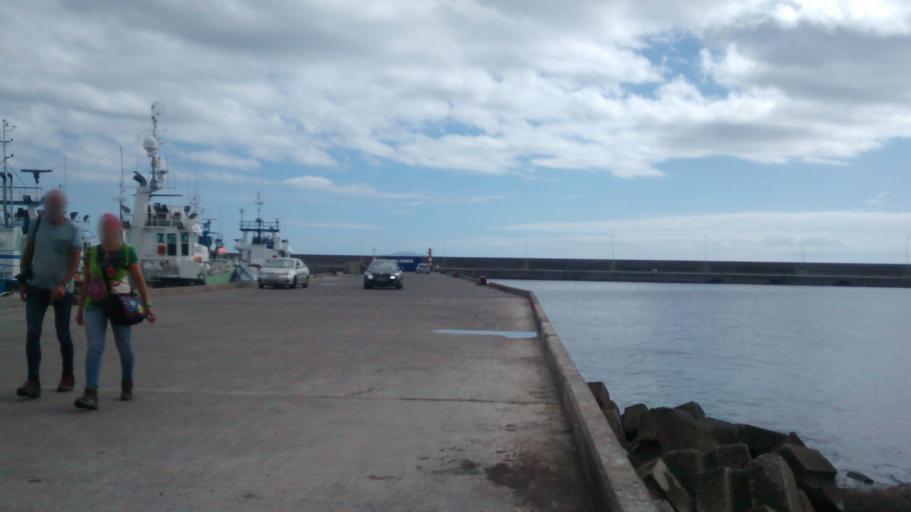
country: PT
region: Madeira
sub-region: Machico
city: Canical
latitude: 32.7359
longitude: -16.7356
